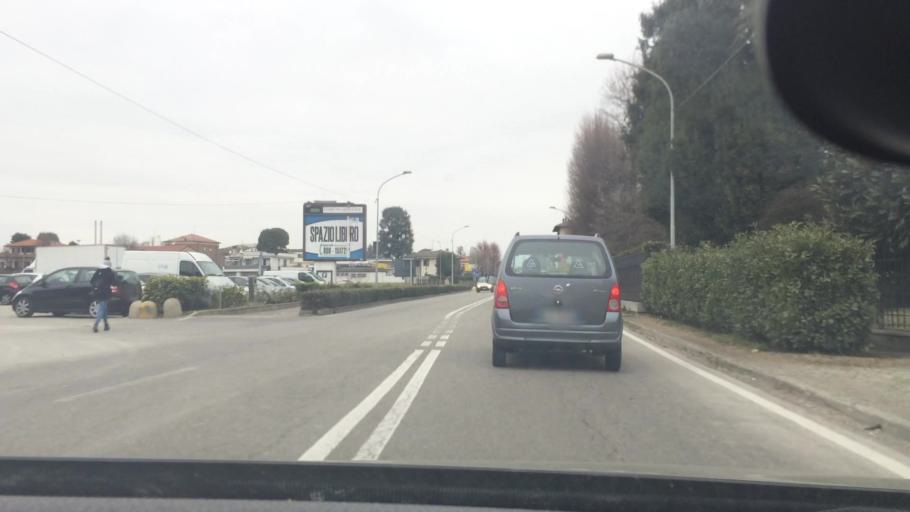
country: IT
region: Lombardy
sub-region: Provincia di Monza e Brianza
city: Lentate sul Seveso
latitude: 45.6774
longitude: 9.1154
